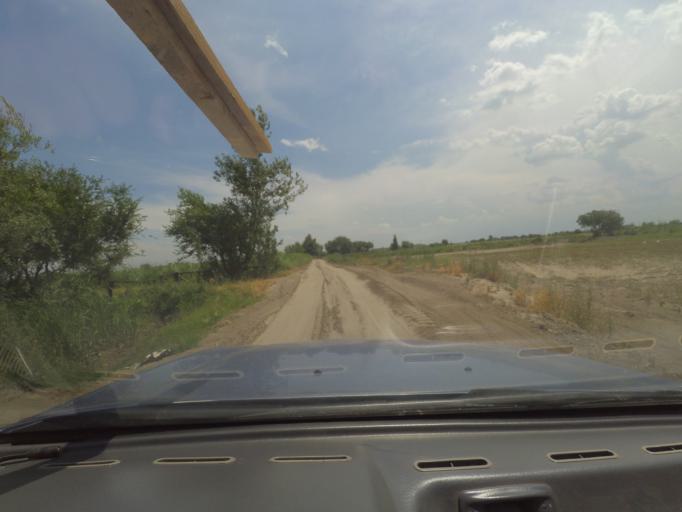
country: TJ
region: Viloyati Sughd
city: Buston
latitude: 40.5498
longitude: 69.0775
